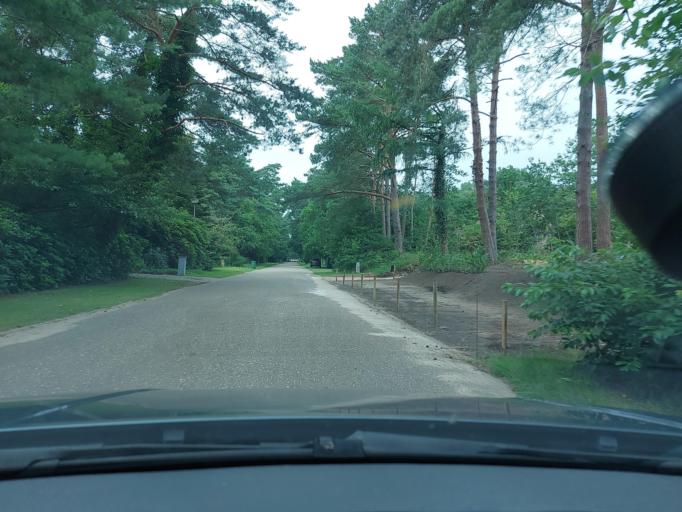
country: BE
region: Flanders
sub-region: Provincie Antwerpen
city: Balen
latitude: 51.1962
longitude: 5.2018
